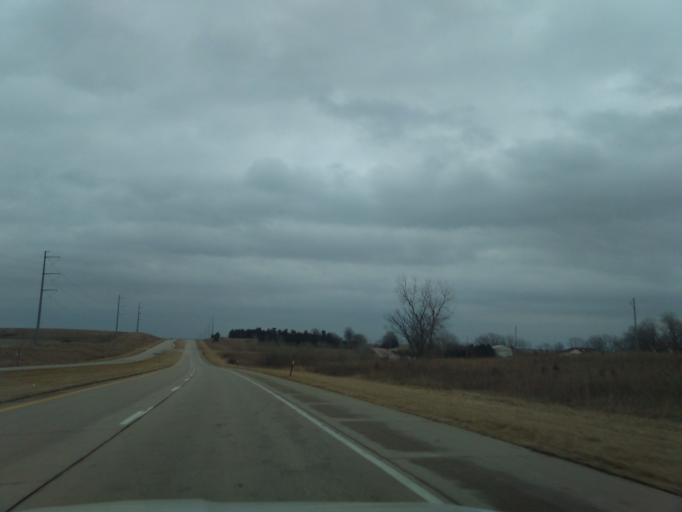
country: US
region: Nebraska
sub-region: Otoe County
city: Syracuse
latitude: 40.6686
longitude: -96.1124
